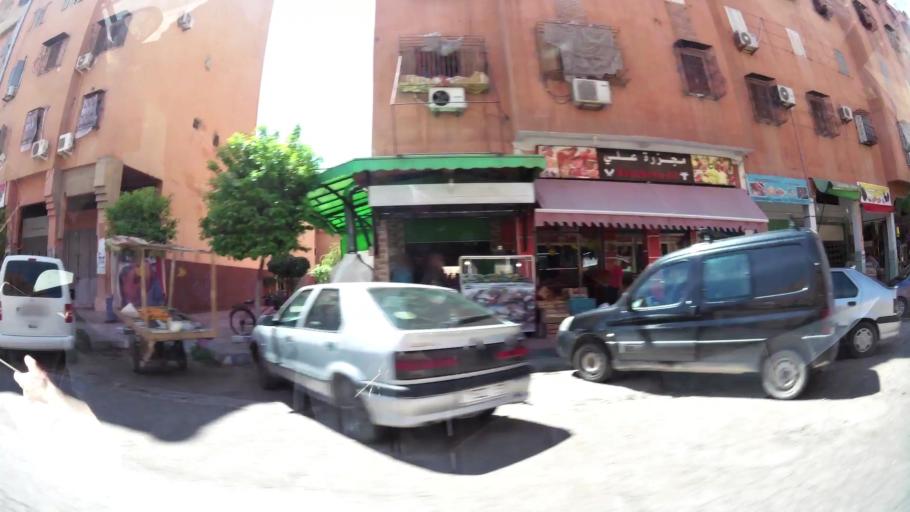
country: MA
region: Marrakech-Tensift-Al Haouz
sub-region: Marrakech
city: Marrakesh
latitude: 31.6455
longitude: -8.0654
